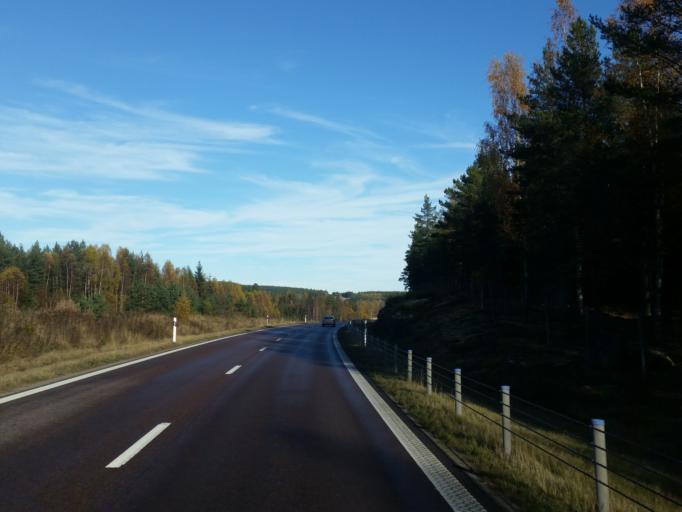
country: SE
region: Dalarna
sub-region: Borlange Kommun
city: Ornas
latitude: 60.5367
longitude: 15.5560
